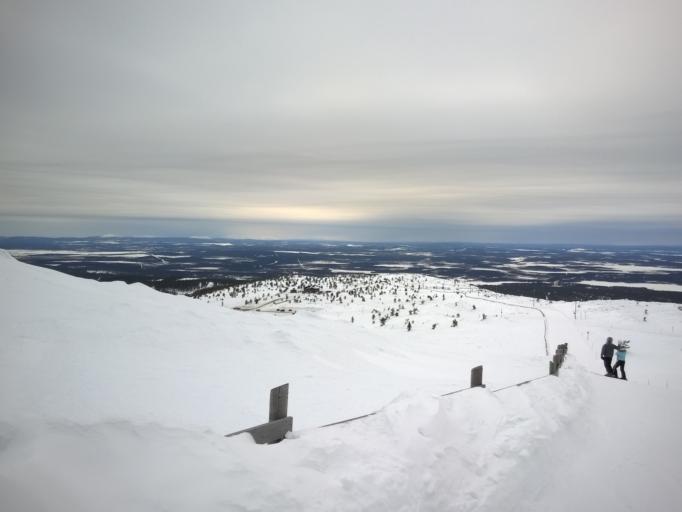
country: FI
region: Lapland
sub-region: Tunturi-Lappi
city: Kittilae
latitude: 67.7863
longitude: 24.8570
